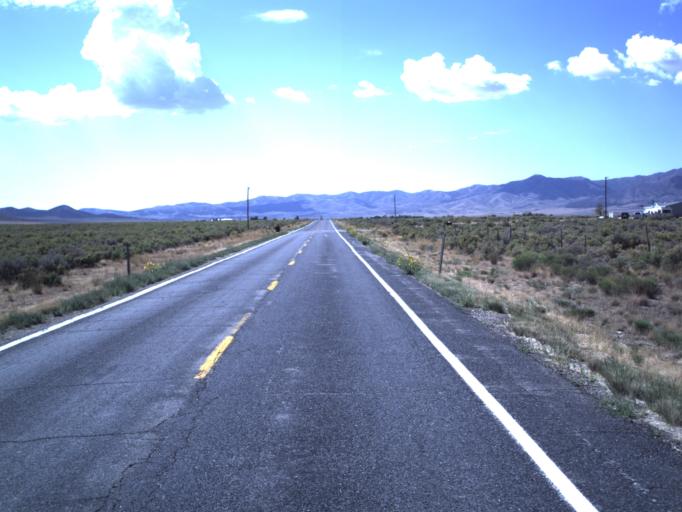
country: US
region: Utah
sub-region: Tooele County
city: Tooele
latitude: 40.1211
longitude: -112.4308
